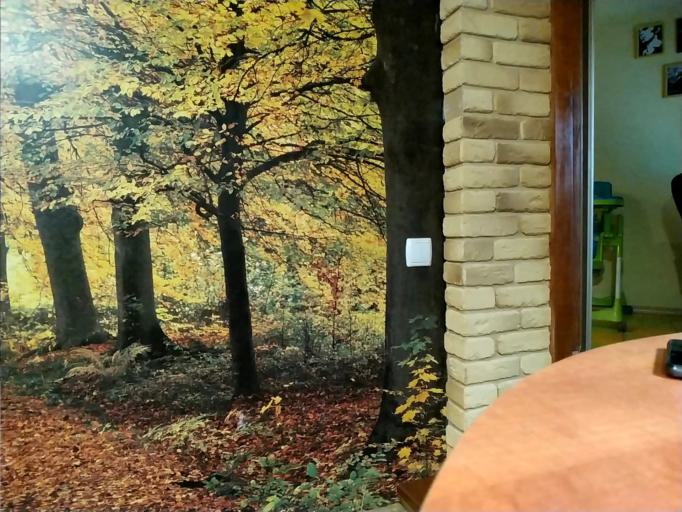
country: BY
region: Minsk
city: Il'ya
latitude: 54.4237
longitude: 27.5078
